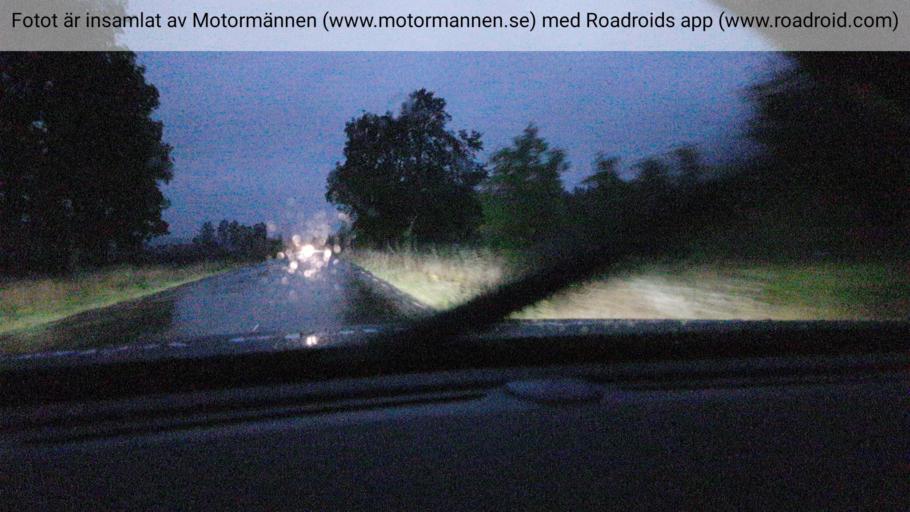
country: SE
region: Vaestra Goetaland
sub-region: Skovde Kommun
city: Skultorp
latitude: 58.2595
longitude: 13.7758
